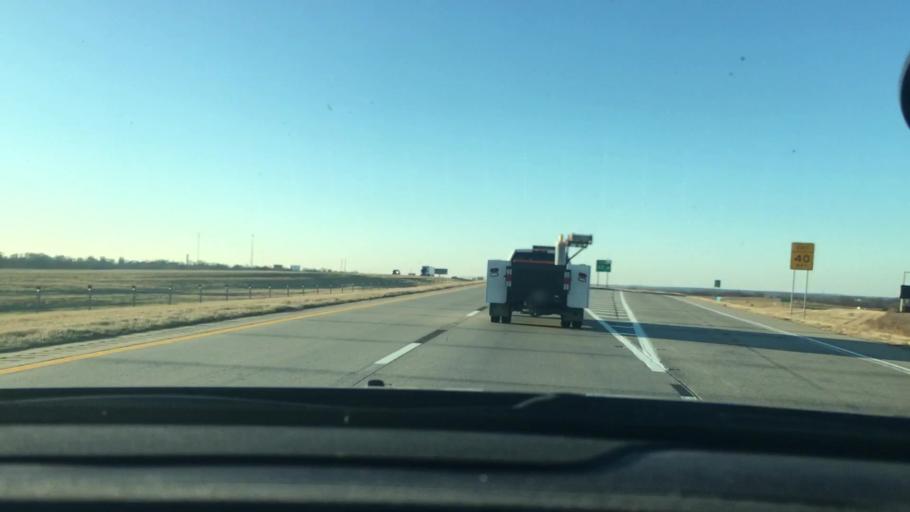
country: US
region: Oklahoma
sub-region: Carter County
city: Ardmore
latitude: 34.3360
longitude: -97.1513
